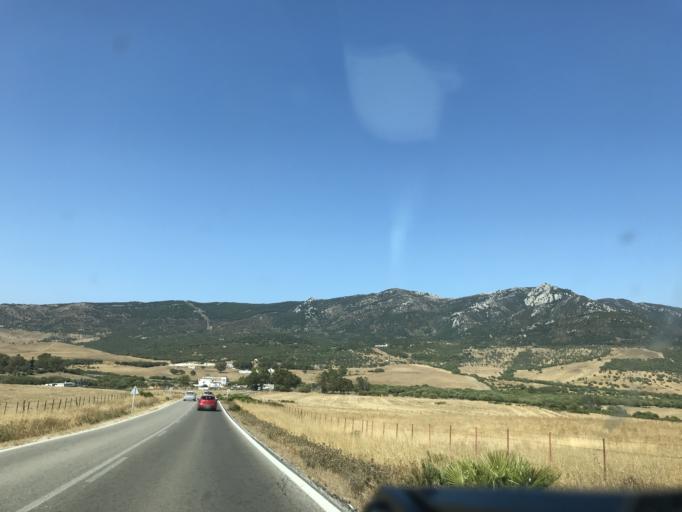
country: ES
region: Andalusia
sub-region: Provincia de Cadiz
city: Zahara de los Atunes
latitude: 36.1059
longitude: -5.7143
